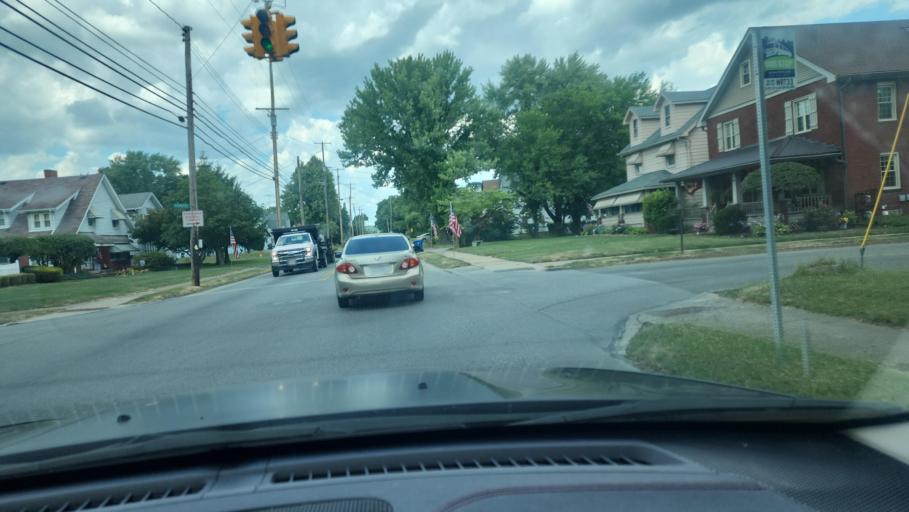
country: US
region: Ohio
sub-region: Mahoning County
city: Struthers
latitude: 41.0480
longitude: -80.5917
